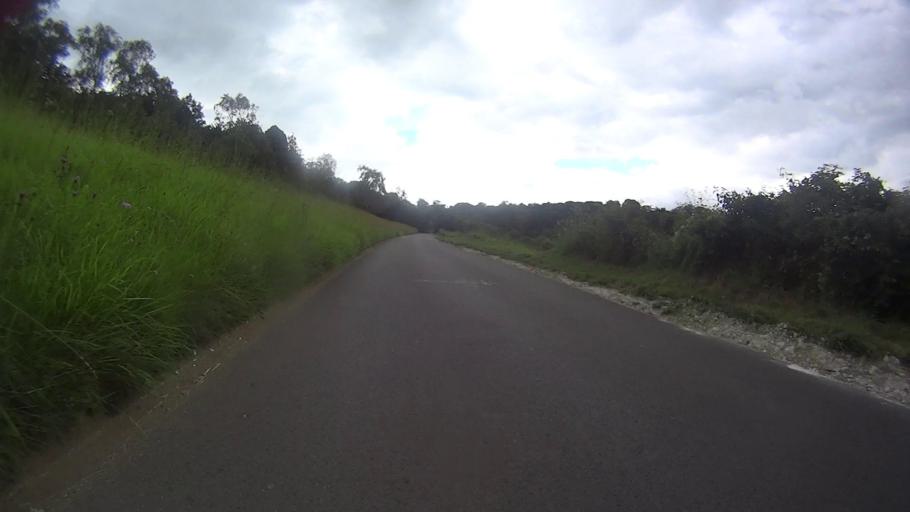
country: GB
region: England
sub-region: Surrey
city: Mickleham
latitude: 51.2543
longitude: -0.3127
